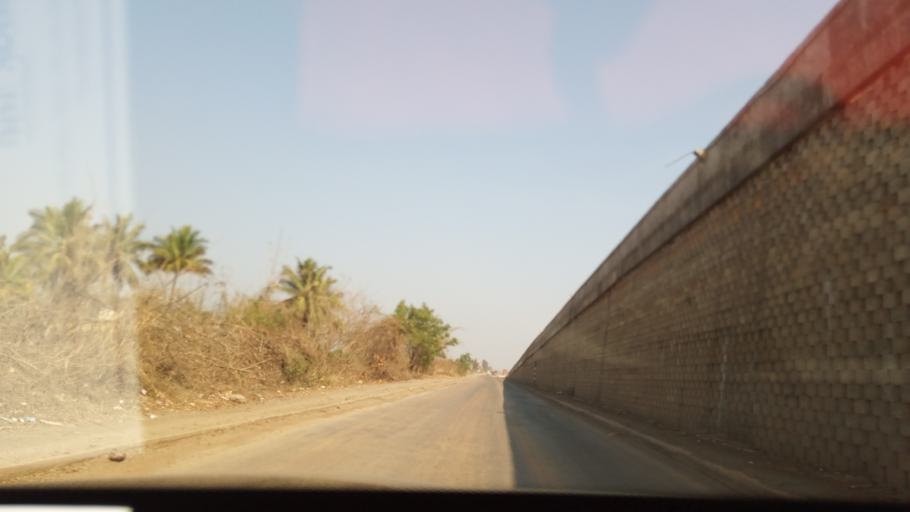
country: IN
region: Karnataka
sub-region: Haveri
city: Shiggaon
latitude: 15.0402
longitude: 75.1719
